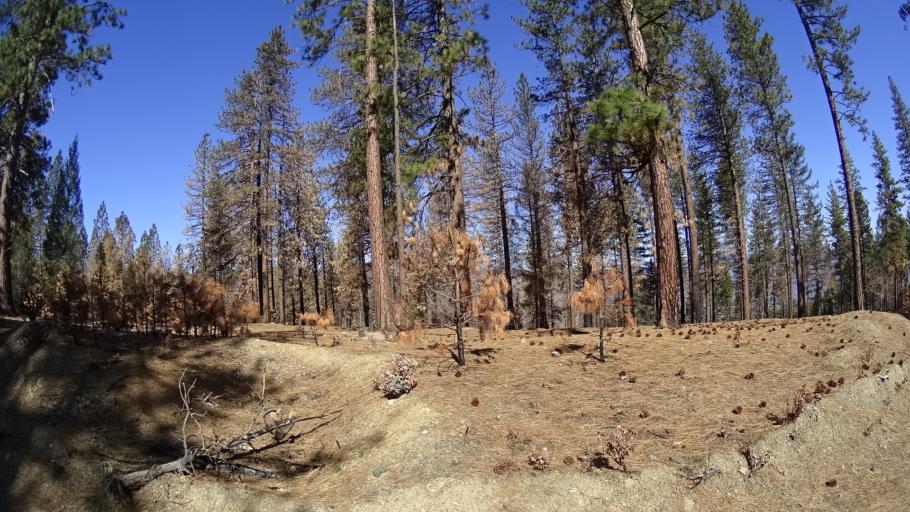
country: US
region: California
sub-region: Tehama County
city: Rancho Tehama Reserve
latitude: 39.6536
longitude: -122.7254
